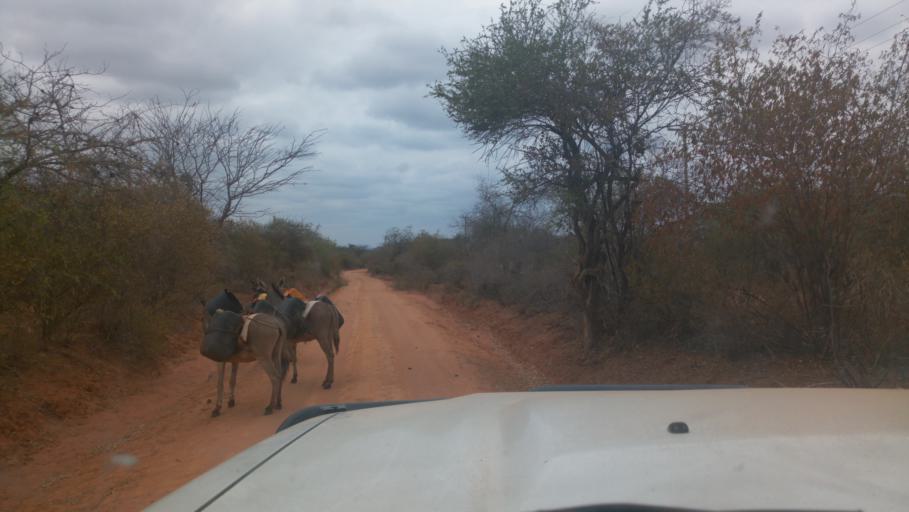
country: KE
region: Makueni
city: Wote
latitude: -1.8544
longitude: 37.9942
